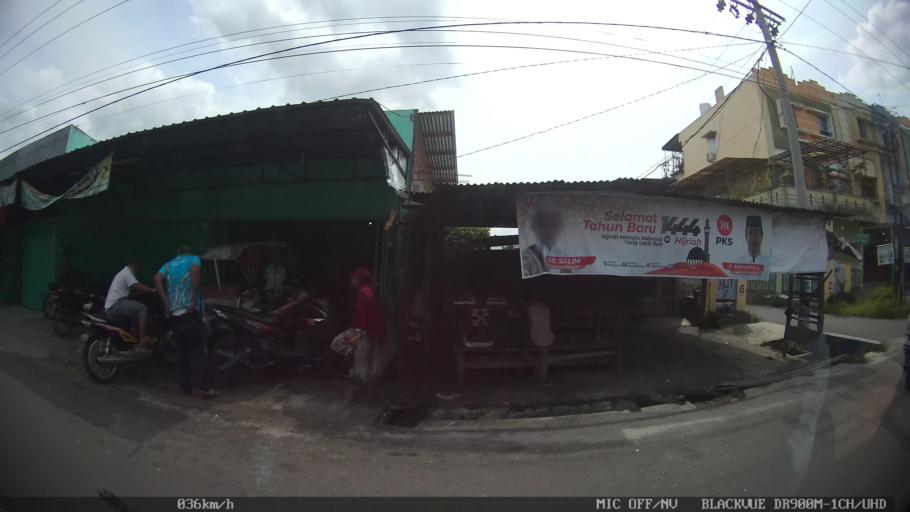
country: ID
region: North Sumatra
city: Percut
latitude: 3.5783
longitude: 98.8649
